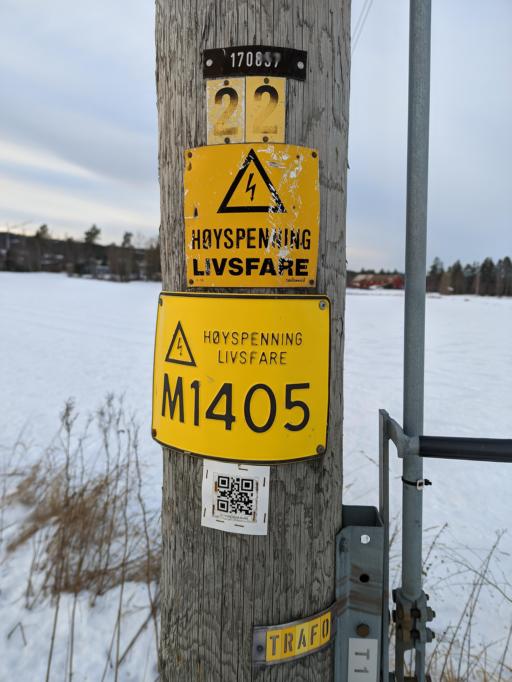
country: NO
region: Akershus
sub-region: Nannestad
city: Teigebyen
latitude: 60.1657
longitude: 10.9982
